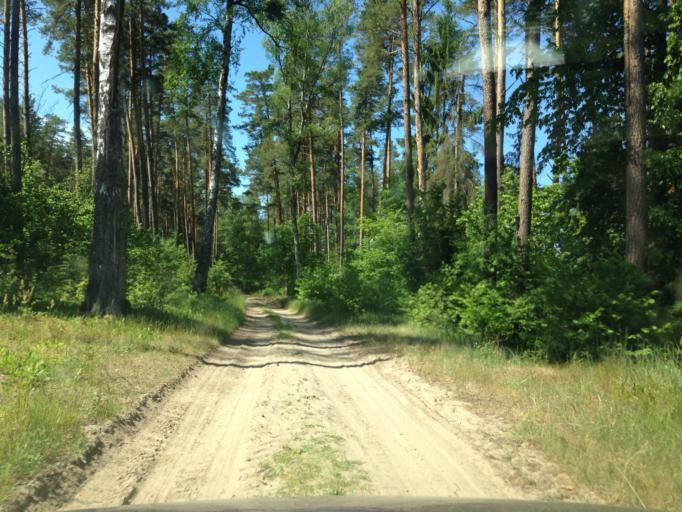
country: PL
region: Kujawsko-Pomorskie
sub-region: Powiat brodnicki
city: Bartniczka
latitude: 53.2646
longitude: 19.5521
